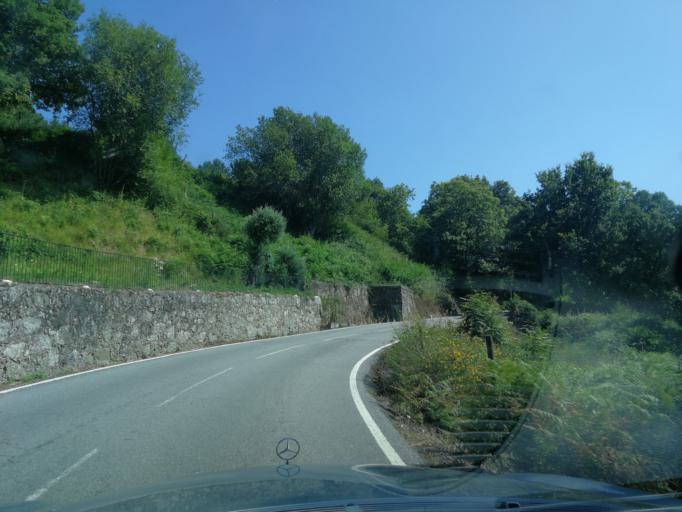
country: PT
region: Braga
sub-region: Braga
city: Adaufe
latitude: 41.5764
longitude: -8.3873
